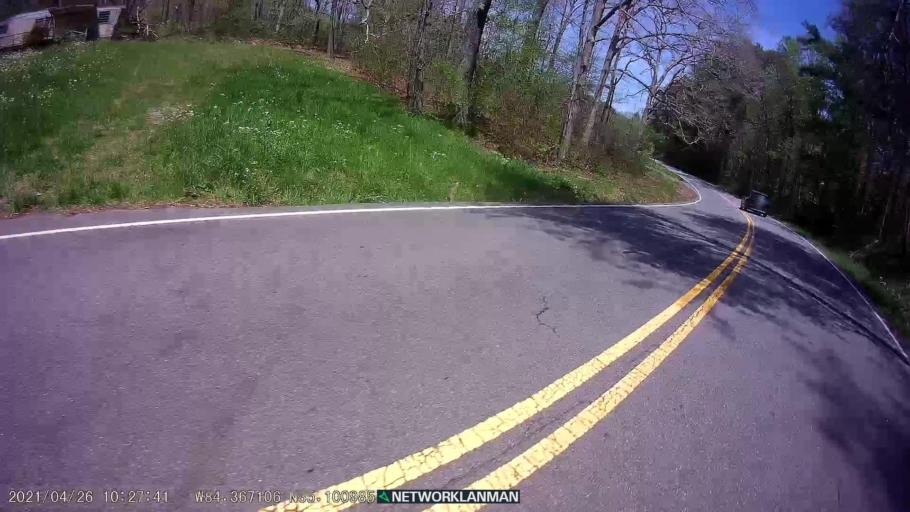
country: US
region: Georgia
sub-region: Fannin County
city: McCaysville
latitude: 35.1011
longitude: -84.3670
